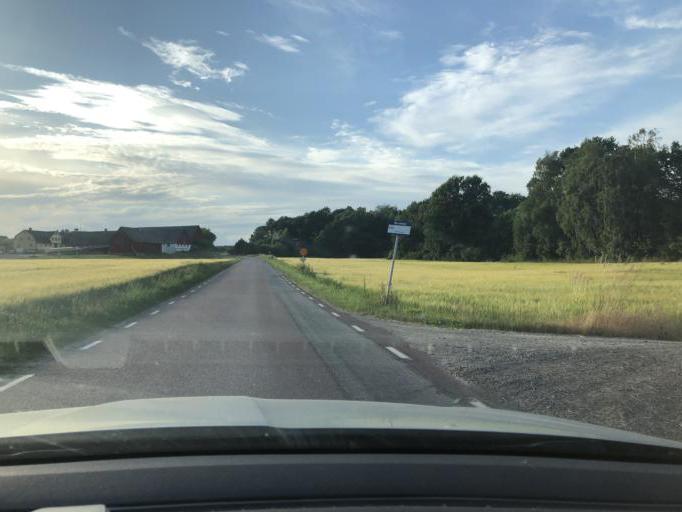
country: SE
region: Blekinge
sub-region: Solvesborgs Kommun
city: Soelvesborg
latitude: 56.1178
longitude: 14.6223
